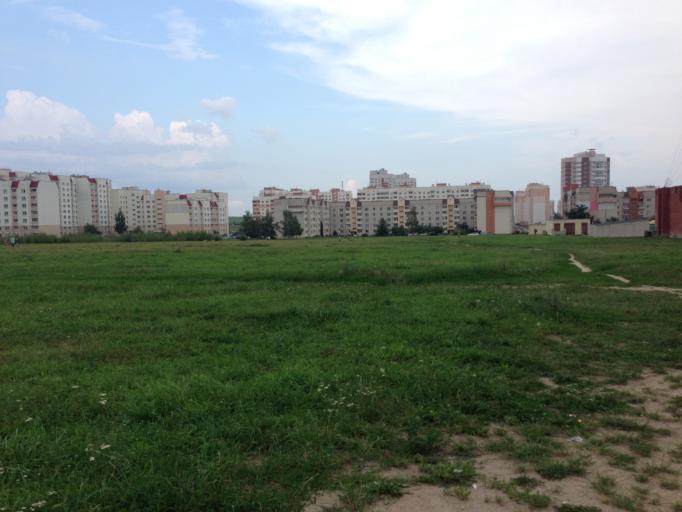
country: BY
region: Grodnenskaya
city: Hrodna
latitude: 53.7128
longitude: 23.8527
